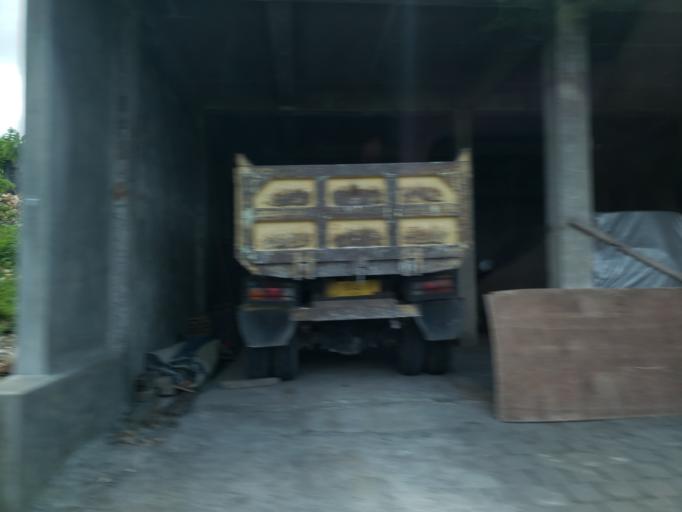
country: ID
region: Bali
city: Kangin
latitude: -8.8429
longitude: 115.1486
